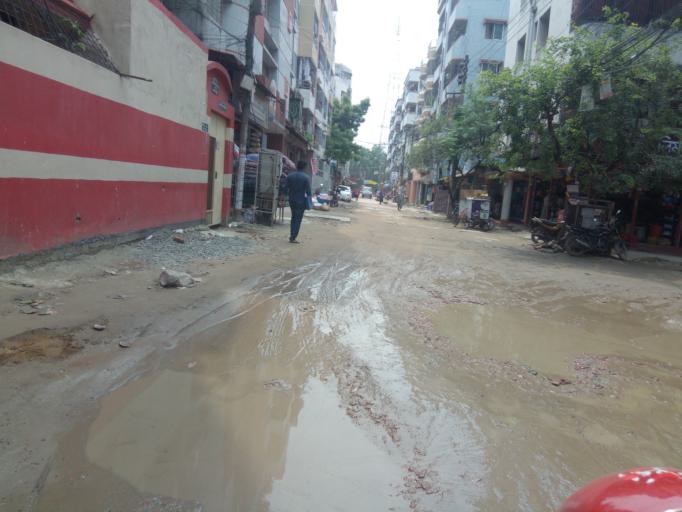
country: BD
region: Dhaka
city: Paltan
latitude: 23.7637
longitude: 90.4262
